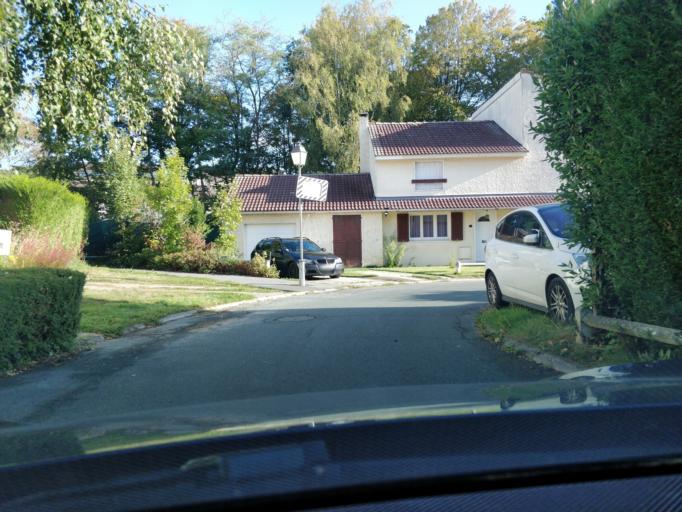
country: FR
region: Ile-de-France
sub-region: Departement de l'Essonne
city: Forges-les-Bains
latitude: 48.6286
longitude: 2.0916
